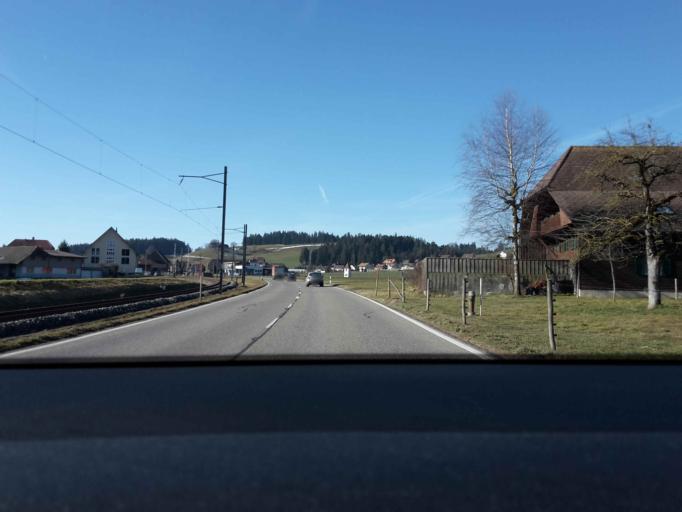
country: CH
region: Bern
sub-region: Emmental District
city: Durrenroth
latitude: 47.0827
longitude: 7.7525
